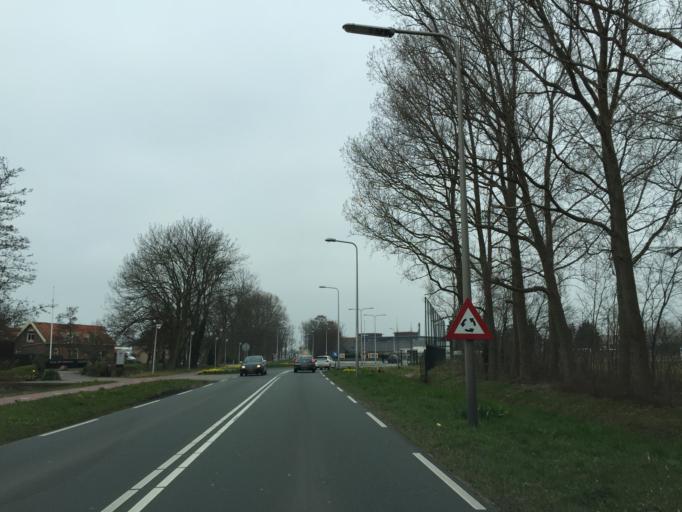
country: NL
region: South Holland
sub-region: Gemeente Westland
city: Naaldwijk
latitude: 51.9821
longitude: 4.2072
